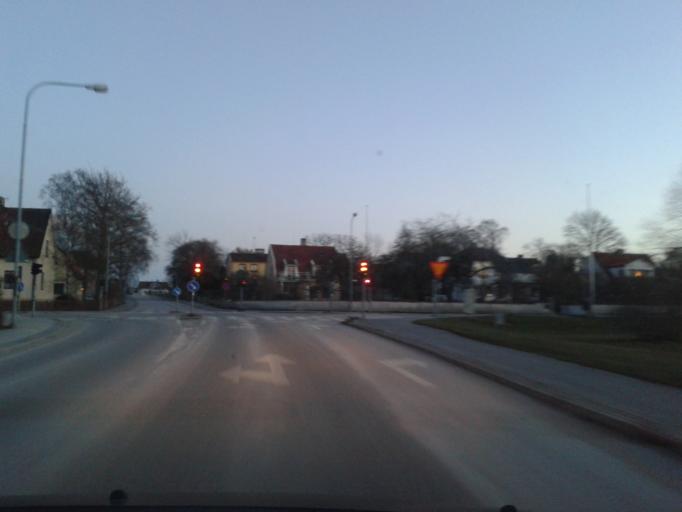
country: SE
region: Gotland
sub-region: Gotland
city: Visby
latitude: 57.6268
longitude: 18.2819
